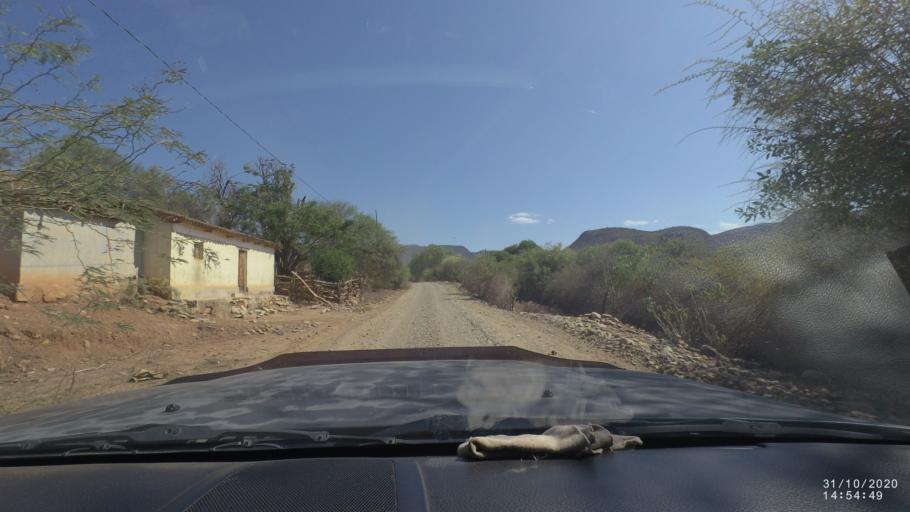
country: BO
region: Cochabamba
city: Aiquile
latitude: -18.2289
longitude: -64.8577
